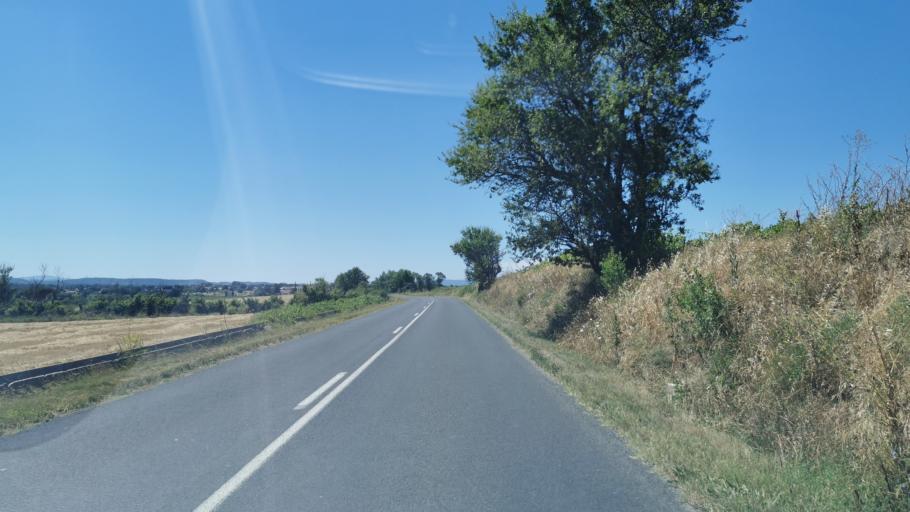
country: FR
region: Languedoc-Roussillon
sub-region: Departement de l'Aude
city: Coursan
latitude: 43.2322
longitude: 3.0873
